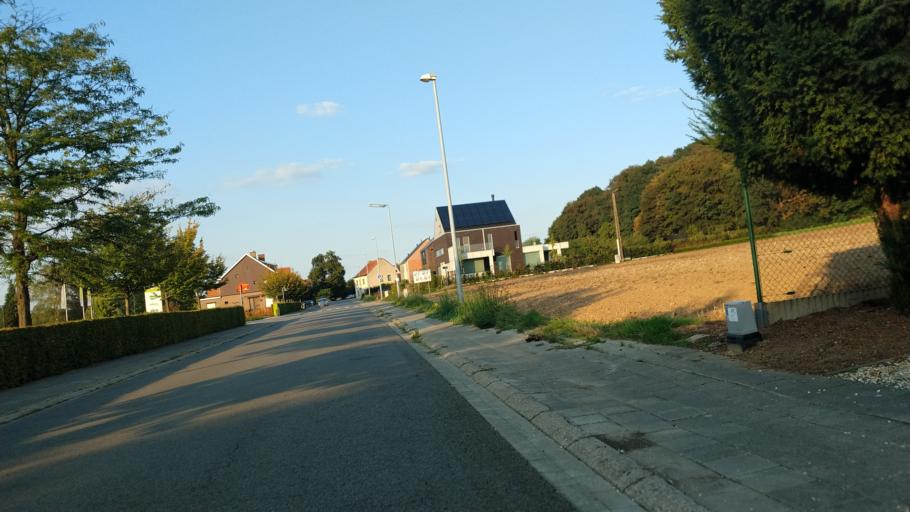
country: BE
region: Flanders
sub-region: Provincie Vlaams-Brabant
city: Holsbeek
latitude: 50.8849
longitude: 4.7498
